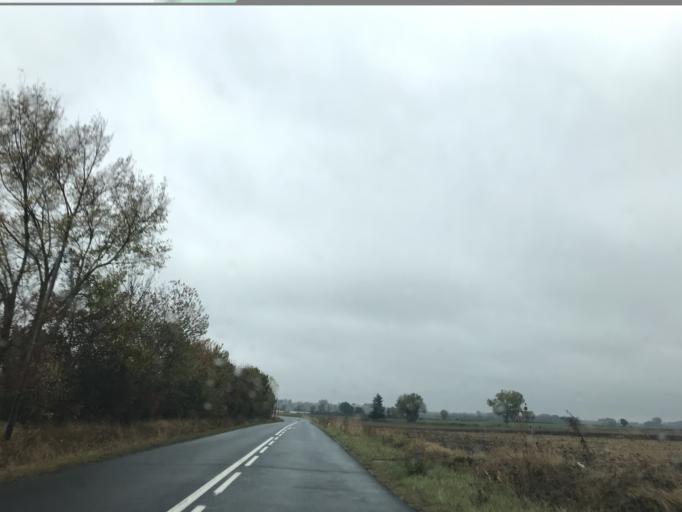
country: FR
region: Auvergne
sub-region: Departement du Puy-de-Dome
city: Vertaizon
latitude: 45.7811
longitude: 3.3264
